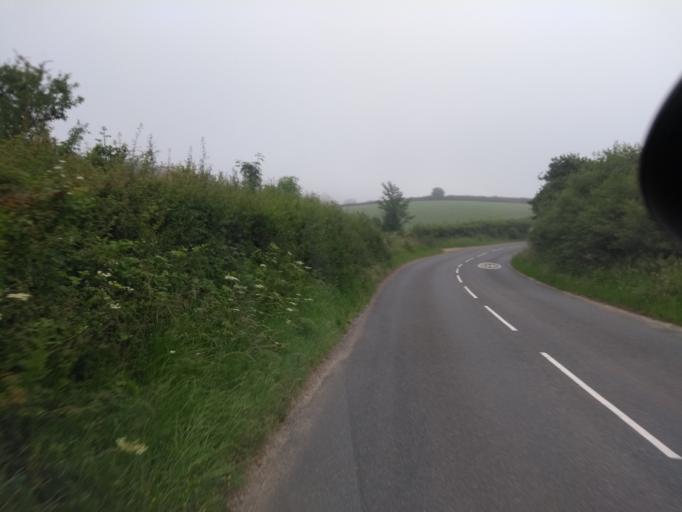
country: GB
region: England
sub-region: Somerset
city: Crewkerne
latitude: 50.8322
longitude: -2.8113
